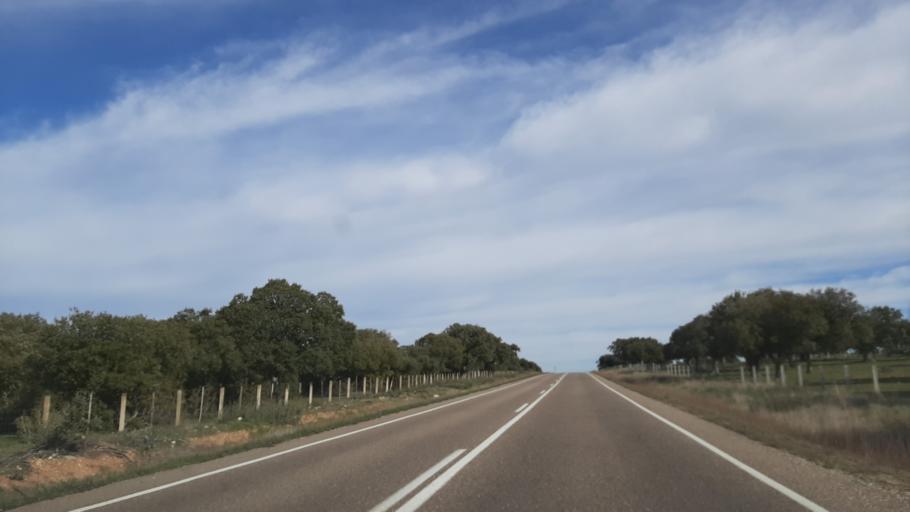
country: ES
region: Castille and Leon
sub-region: Provincia de Salamanca
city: Ledesma
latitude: 41.0897
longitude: -5.9538
